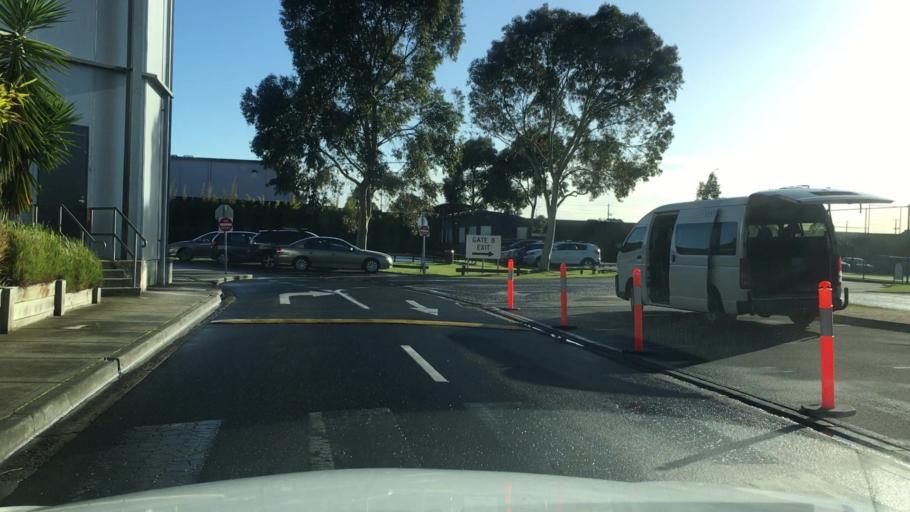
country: AU
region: Victoria
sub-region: Kingston
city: Dingley Village
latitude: -37.9937
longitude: 145.1468
